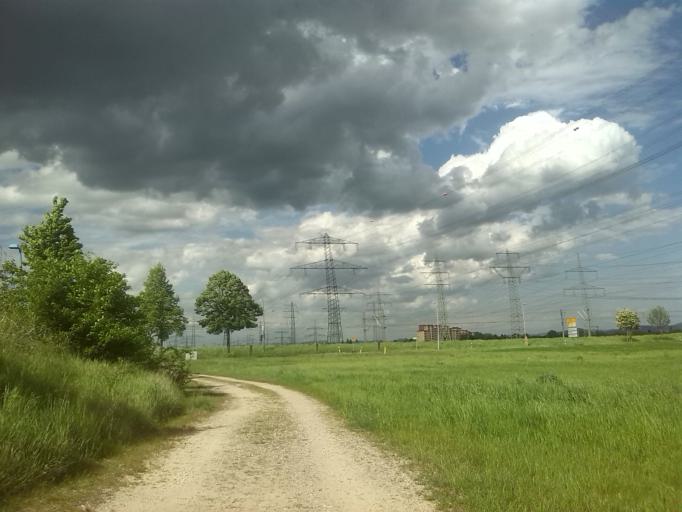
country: DE
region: Baden-Wuerttemberg
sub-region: Karlsruhe Region
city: Ilvesheim
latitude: 49.4735
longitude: 8.5428
